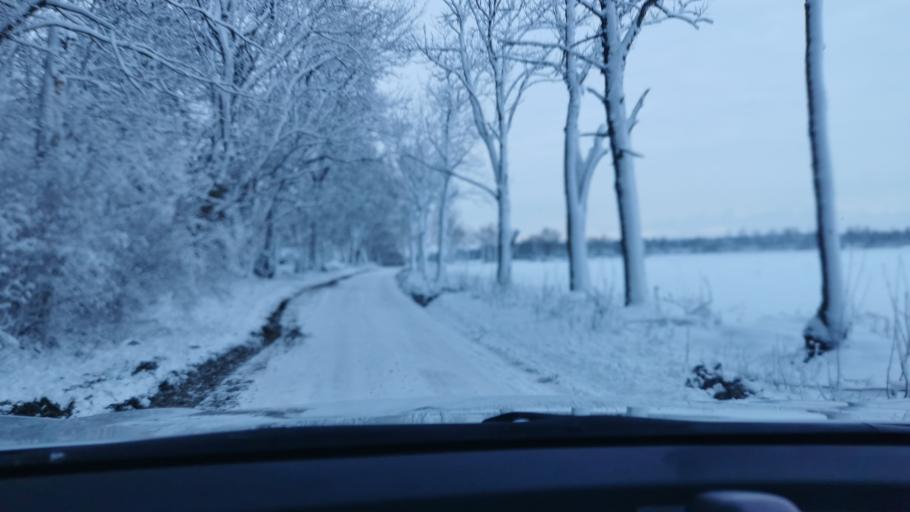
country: EE
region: Laeaene-Virumaa
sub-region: Viru-Nigula vald
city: Kunda
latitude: 59.4930
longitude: 26.4065
